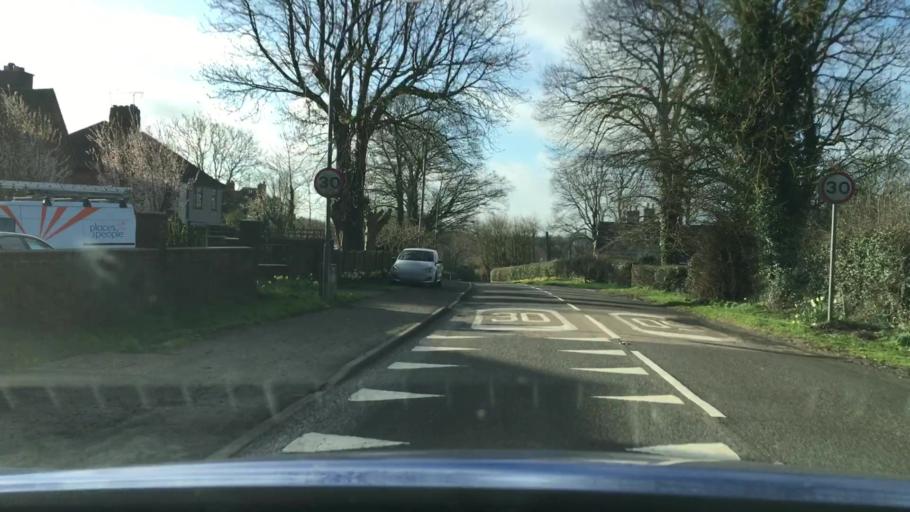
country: GB
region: England
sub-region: Derbyshire
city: Tibshelf
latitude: 53.1526
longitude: -1.3371
